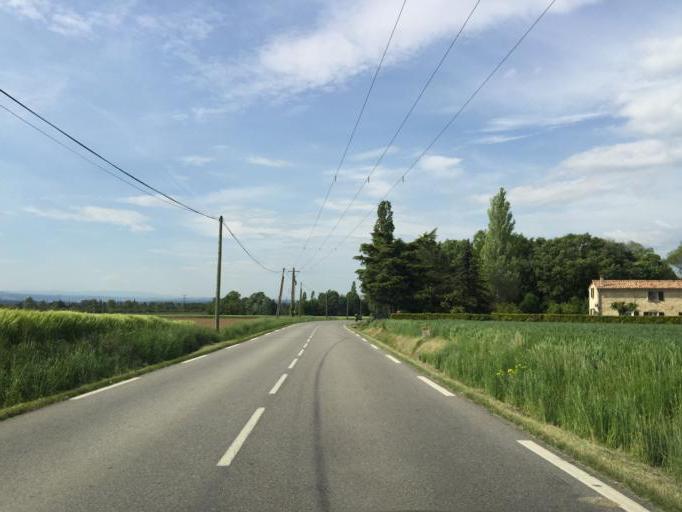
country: FR
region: Rhone-Alpes
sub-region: Departement de la Drome
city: Montmeyran
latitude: 44.8234
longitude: 5.0098
